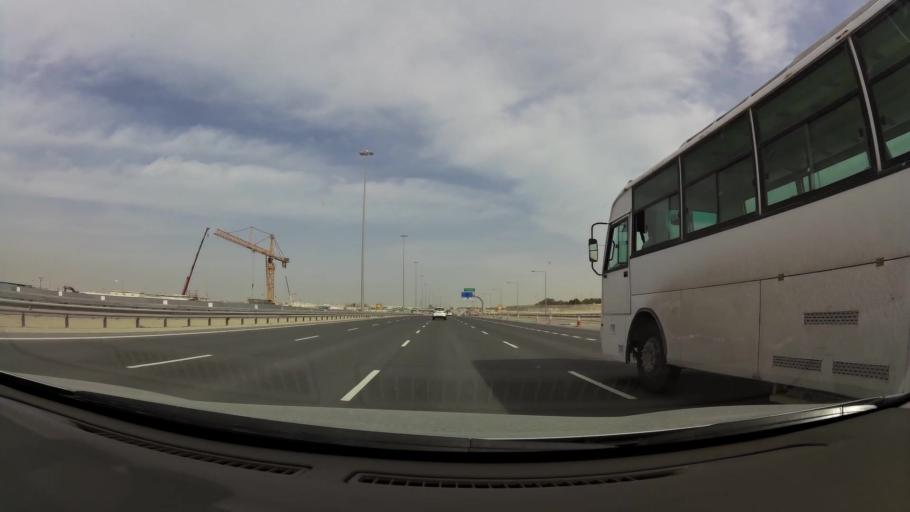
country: QA
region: Baladiyat ar Rayyan
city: Ar Rayyan
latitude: 25.3152
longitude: 51.3693
